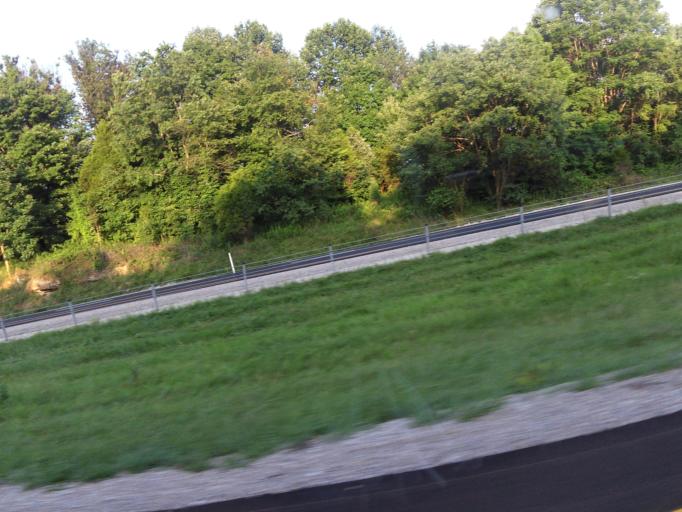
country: US
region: Kentucky
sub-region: Rockcastle County
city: Brodhead
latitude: 37.4349
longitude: -84.3422
